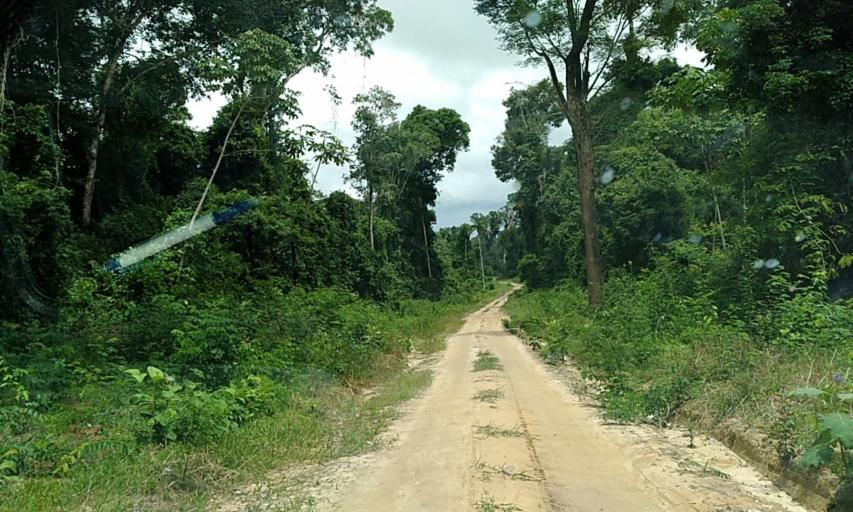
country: BR
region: Para
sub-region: Altamira
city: Altamira
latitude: -3.0533
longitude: -52.9096
